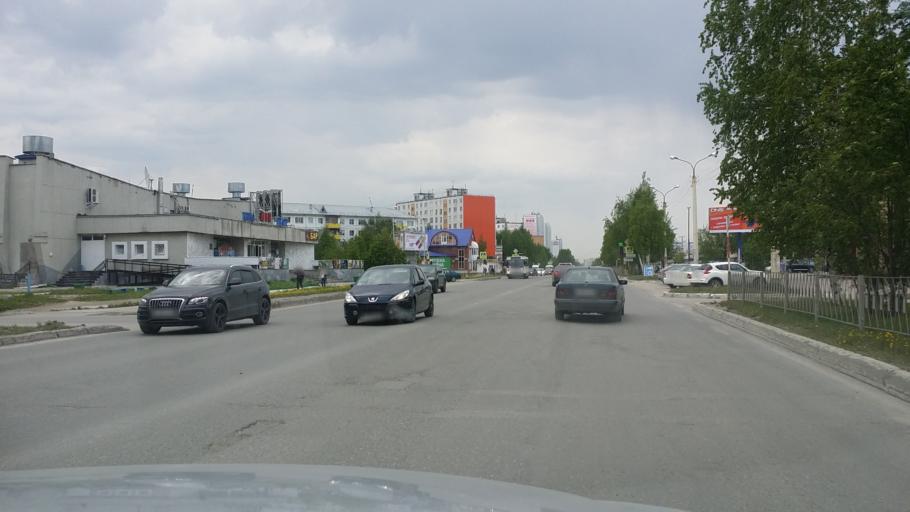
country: RU
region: Khanty-Mansiyskiy Avtonomnyy Okrug
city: Nizhnevartovsk
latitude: 60.9361
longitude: 76.6058
